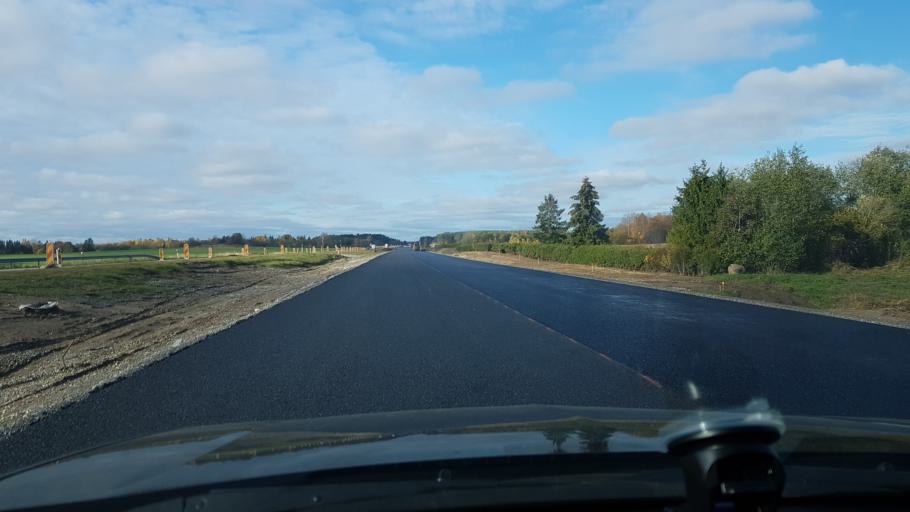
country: EE
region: Laeaene-Virumaa
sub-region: Kadrina vald
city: Kadrina
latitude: 59.4419
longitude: 26.1114
